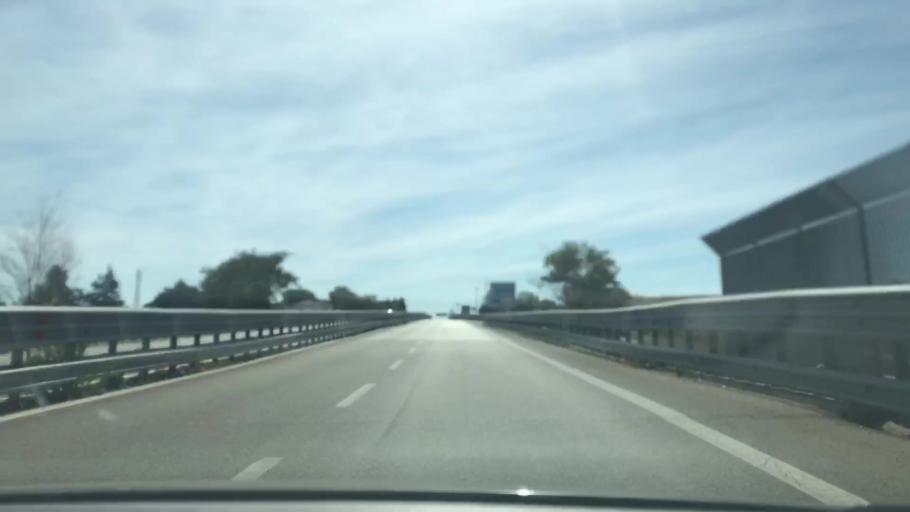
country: IT
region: Basilicate
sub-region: Provincia di Matera
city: Matera
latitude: 40.7079
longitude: 16.5818
